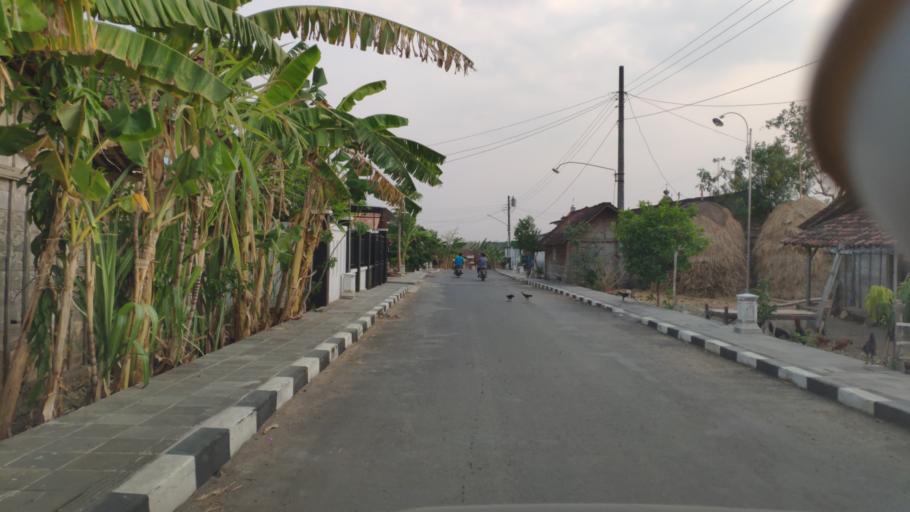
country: ID
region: Central Java
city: Kedungringin
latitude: -6.9879
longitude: 111.3550
